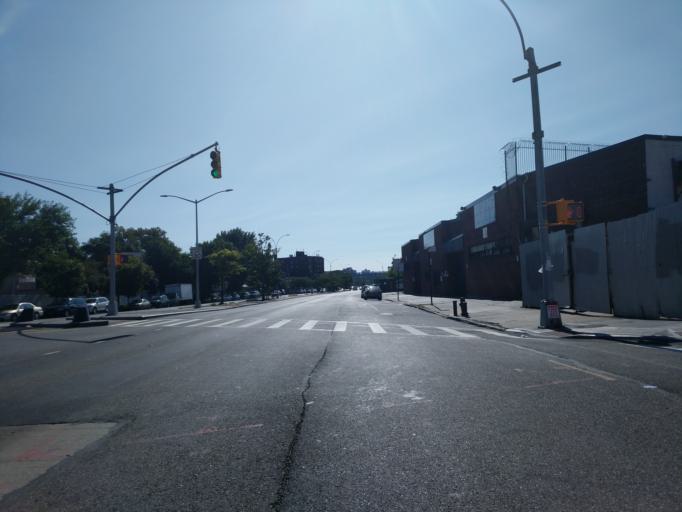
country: US
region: New York
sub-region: Queens County
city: Borough of Queens
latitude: 40.7611
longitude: -73.8645
